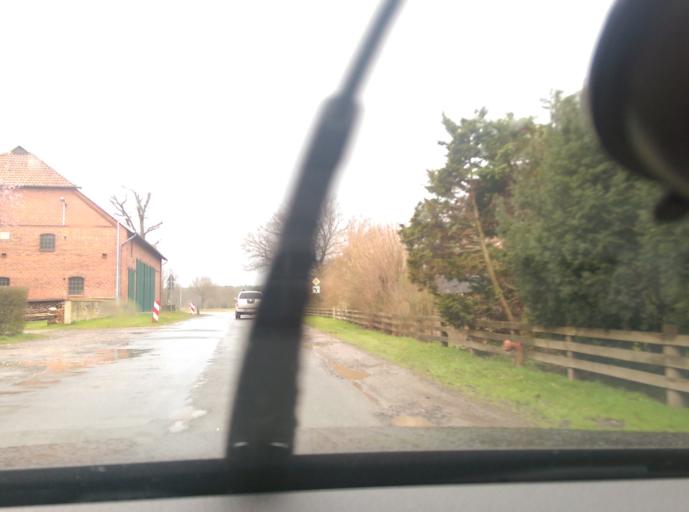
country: DE
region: Lower Saxony
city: Schwarmstedt
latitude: 52.6360
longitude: 9.6069
